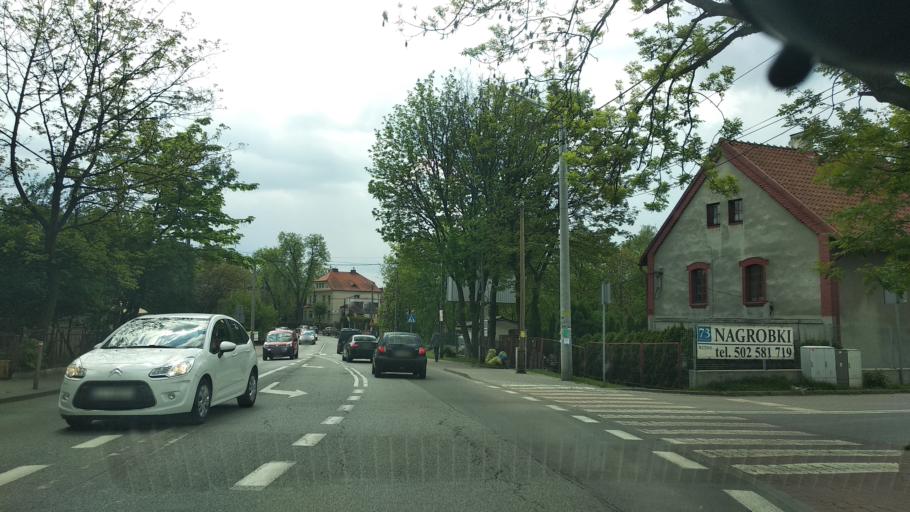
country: PL
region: Silesian Voivodeship
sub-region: Katowice
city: Katowice
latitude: 50.2296
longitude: 18.9708
